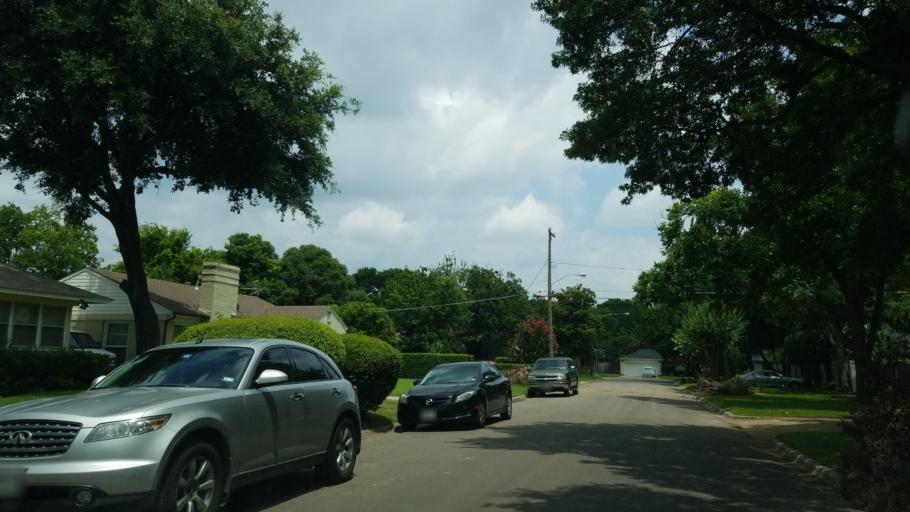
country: US
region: Texas
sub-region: Dallas County
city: University Park
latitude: 32.8386
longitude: -96.8254
